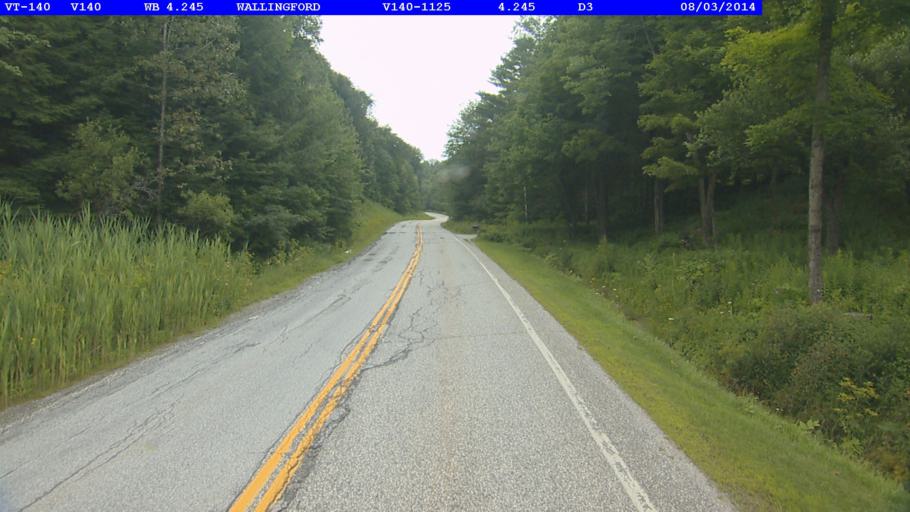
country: US
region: Vermont
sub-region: Rutland County
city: Rutland
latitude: 43.4605
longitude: -72.9062
